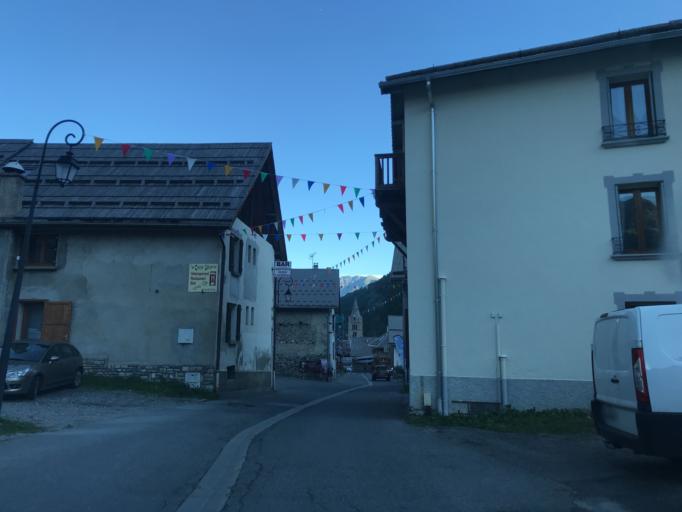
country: FR
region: Provence-Alpes-Cote d'Azur
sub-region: Departement des Hautes-Alpes
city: Guillestre
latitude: 44.7680
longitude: 6.7380
